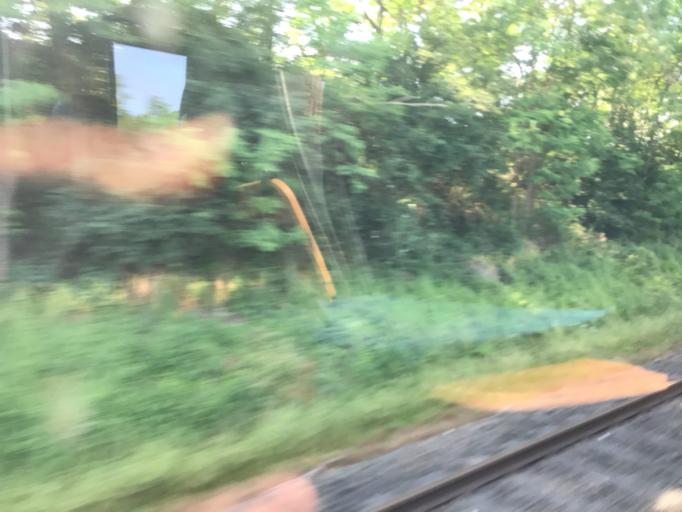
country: DE
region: Rheinland-Pfalz
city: Hintertiefenbach
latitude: 49.7062
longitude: 7.3541
